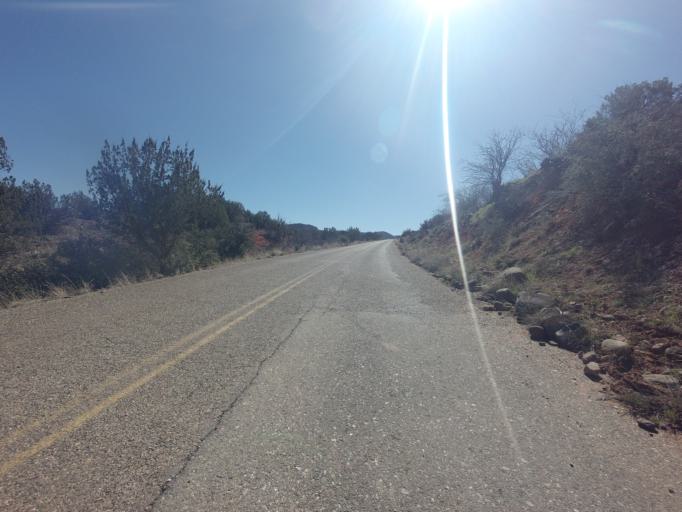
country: US
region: Arizona
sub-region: Yavapai County
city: Lake Montezuma
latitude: 34.6783
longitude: -111.7218
